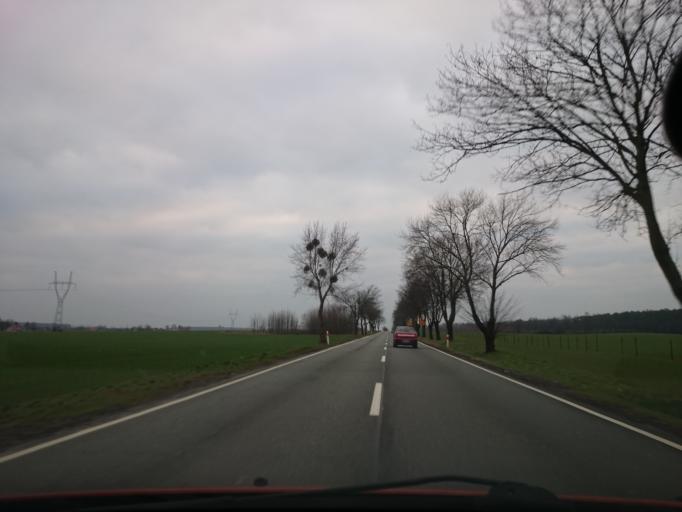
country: PL
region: Opole Voivodeship
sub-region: Powiat nyski
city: Lambinowice
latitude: 50.6087
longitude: 17.5556
